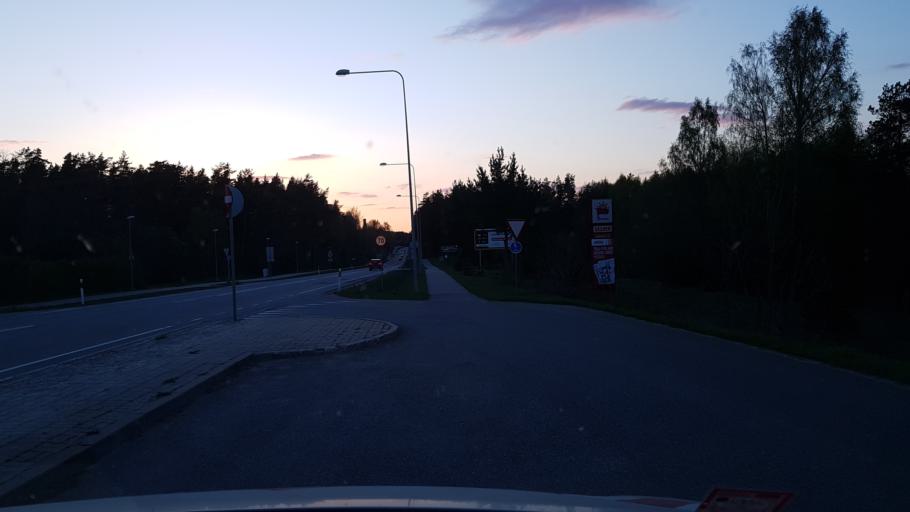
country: EE
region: Vorumaa
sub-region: Voru linn
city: Voru
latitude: 57.8165
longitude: 27.0286
